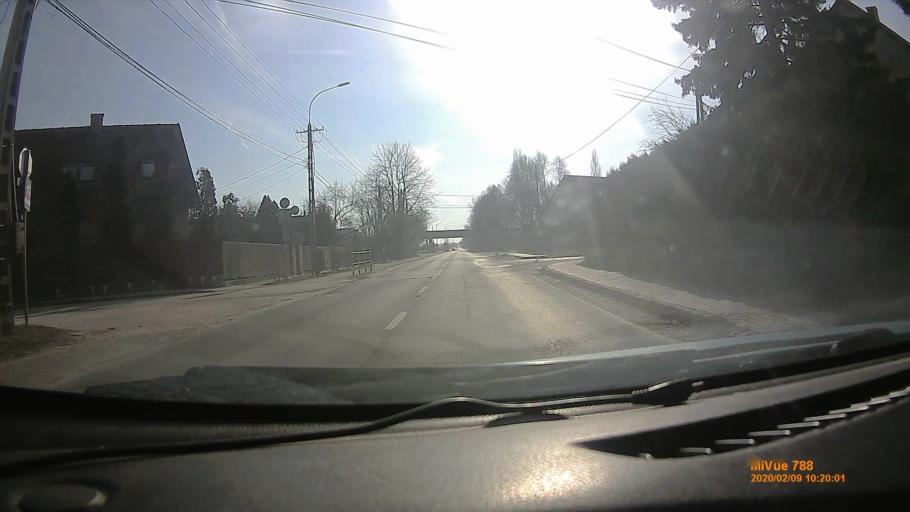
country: HU
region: Pest
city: Dunabogdany
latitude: 47.7957
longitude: 19.0405
